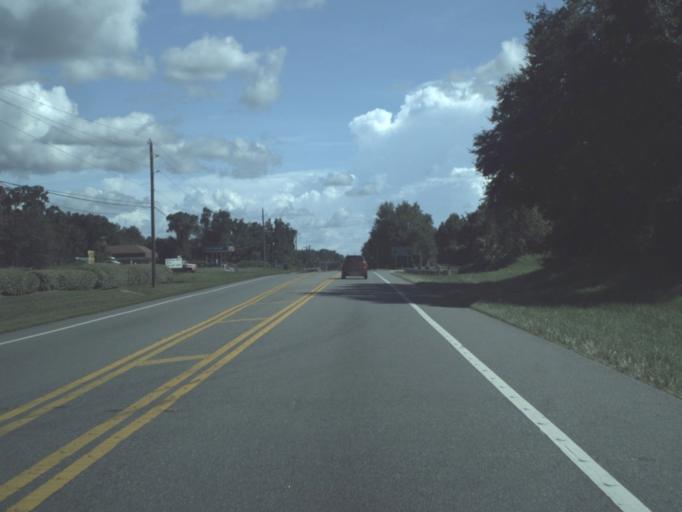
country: US
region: Florida
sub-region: Citrus County
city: Hernando
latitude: 28.8827
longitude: -82.3652
